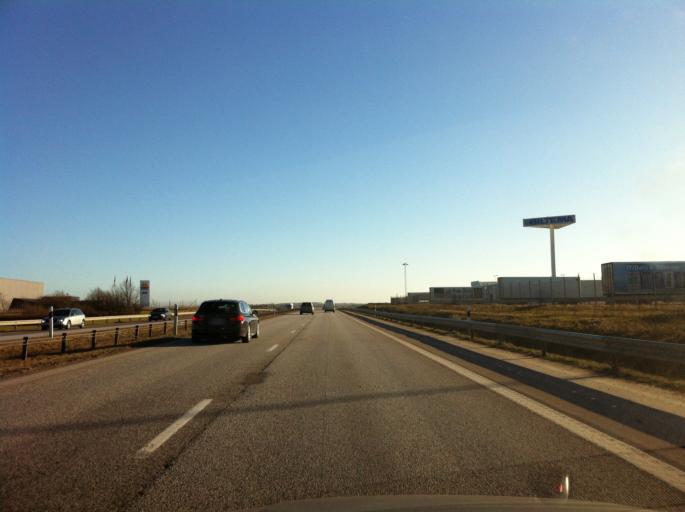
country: SE
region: Skane
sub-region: Angelholms Kommun
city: AEngelholm
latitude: 56.2463
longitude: 12.8986
